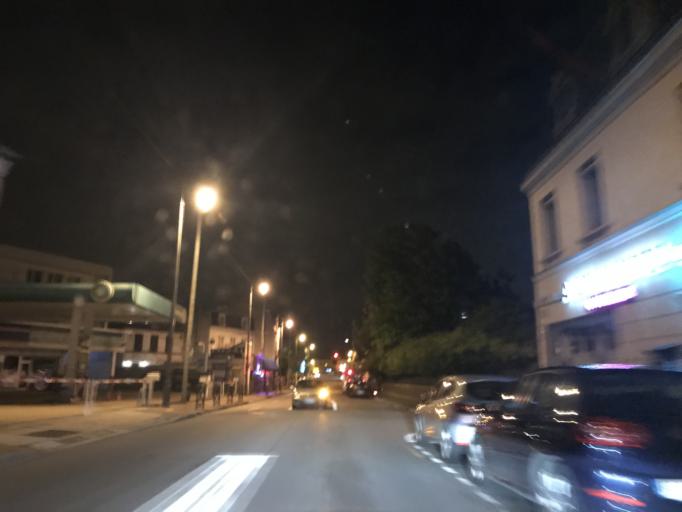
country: FR
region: Ile-de-France
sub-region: Departement des Yvelines
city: Maisons-Laffitte
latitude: 48.9448
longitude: 2.1414
